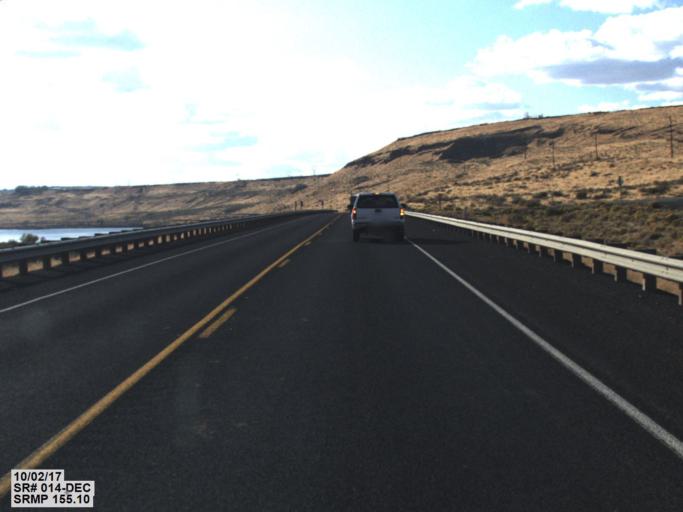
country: US
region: Oregon
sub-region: Morrow County
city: Boardman
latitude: 45.8696
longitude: -119.8248
